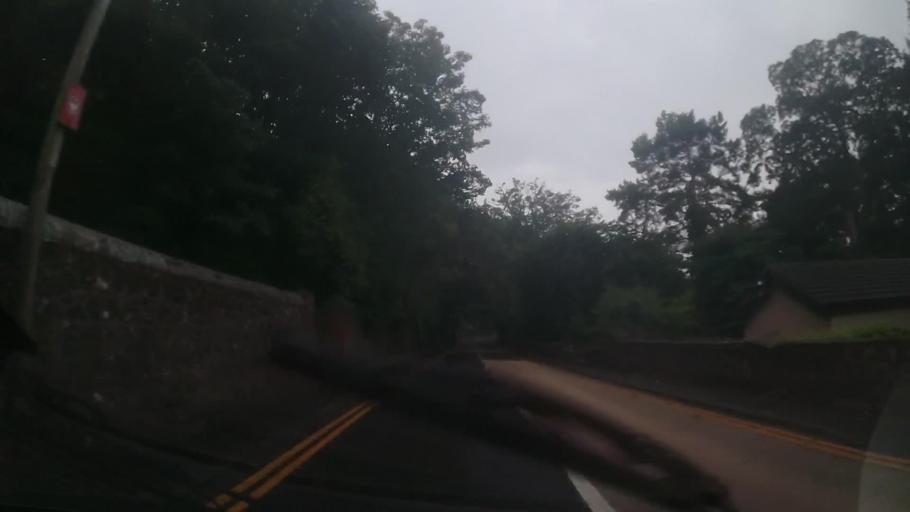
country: GB
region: Scotland
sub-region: North Ayrshire
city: Fairlie
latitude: 55.7564
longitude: -4.8541
